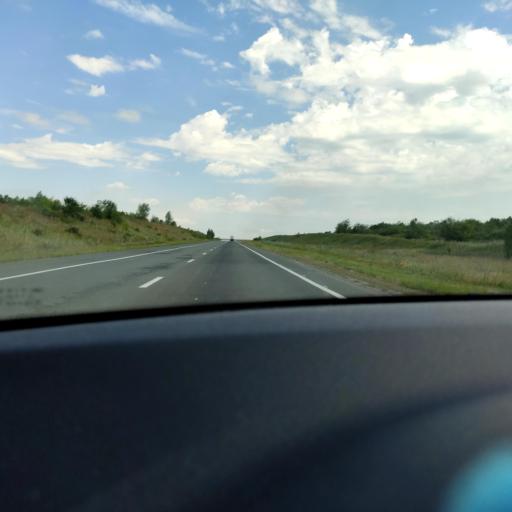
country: RU
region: Samara
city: Petra-Dubrava
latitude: 53.2953
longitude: 50.3959
